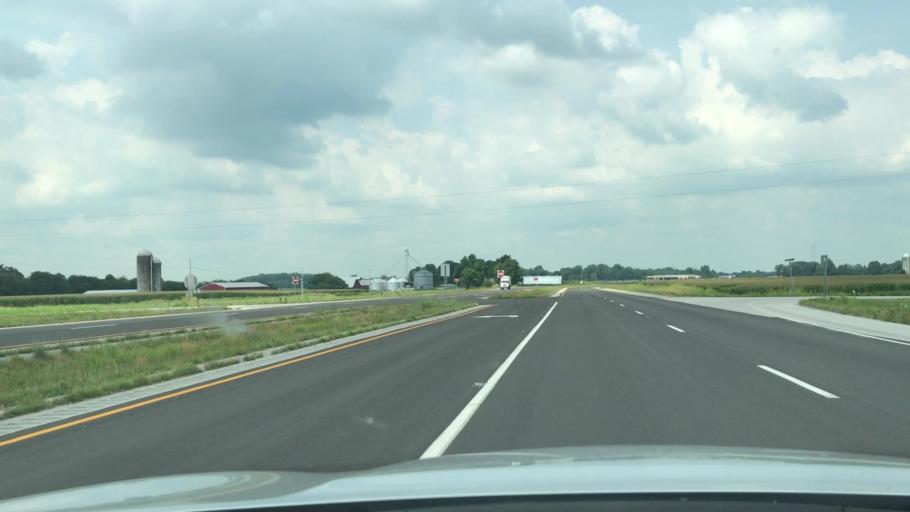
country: US
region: Kentucky
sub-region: Todd County
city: Elkton
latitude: 36.8075
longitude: -87.0489
